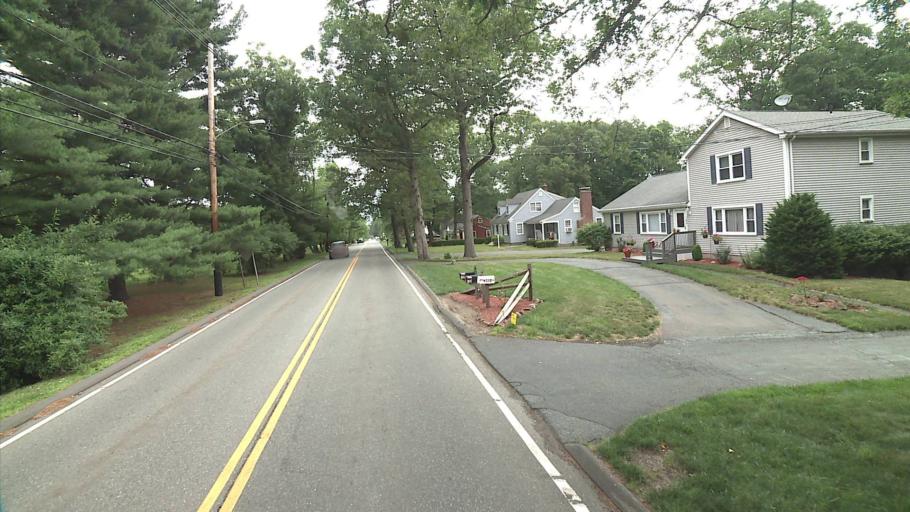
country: US
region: Connecticut
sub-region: New Haven County
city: Wallingford Center
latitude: 41.4424
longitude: -72.8046
